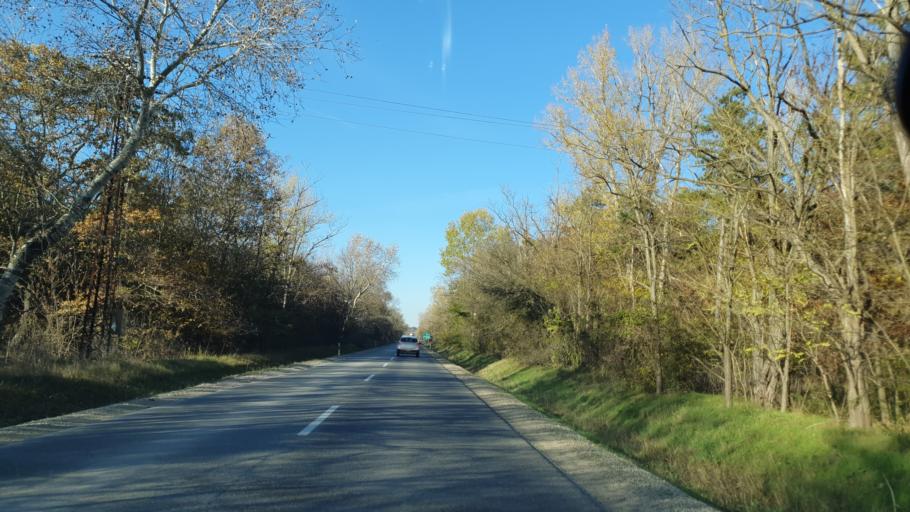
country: HU
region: Fejer
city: Zamoly
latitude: 47.3400
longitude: 18.4045
